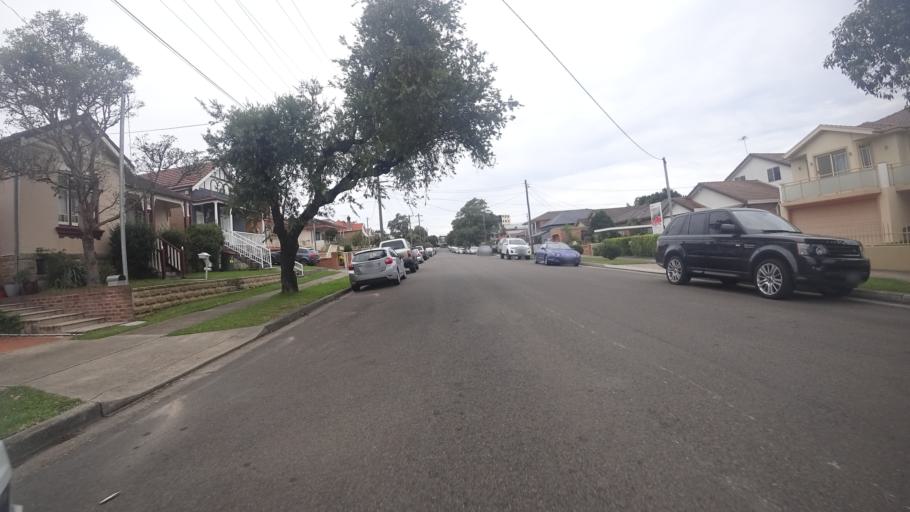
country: AU
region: New South Wales
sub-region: Rockdale
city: Bexley
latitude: -33.9434
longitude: 151.1271
